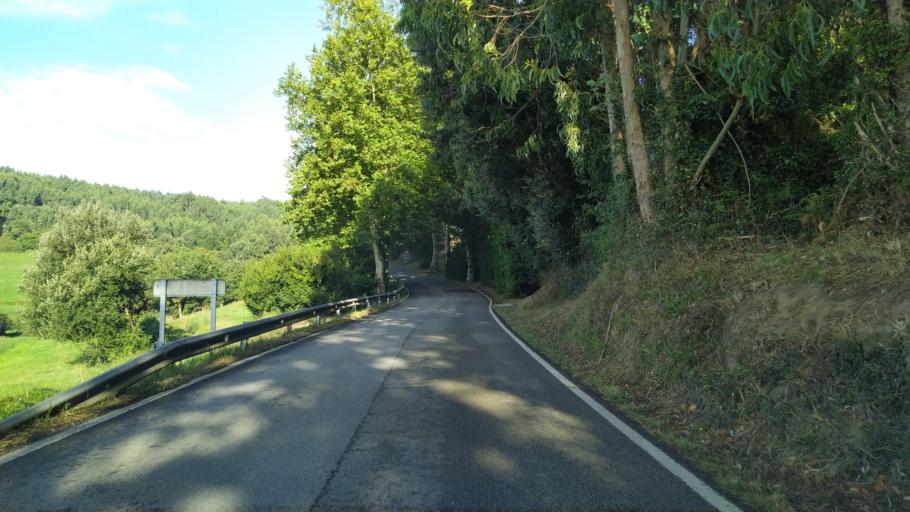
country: ES
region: Cantabria
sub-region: Provincia de Cantabria
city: Santa Cruz de Bezana
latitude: 43.4488
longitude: -3.9260
